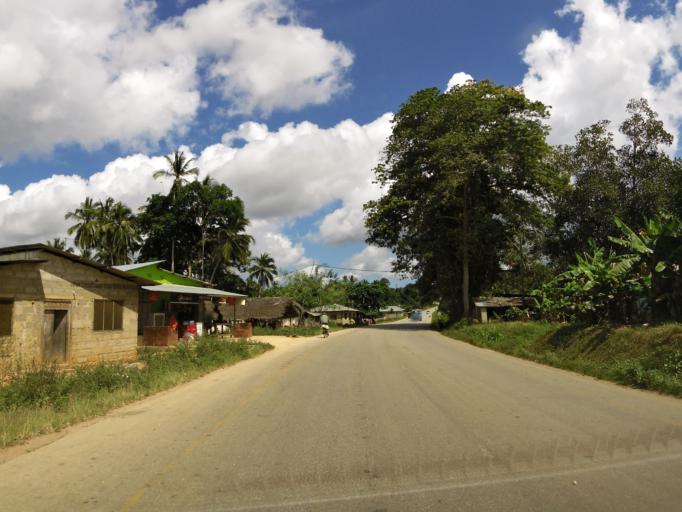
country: TZ
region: Zanzibar Central/South
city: Koani
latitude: -6.1349
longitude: 39.2941
